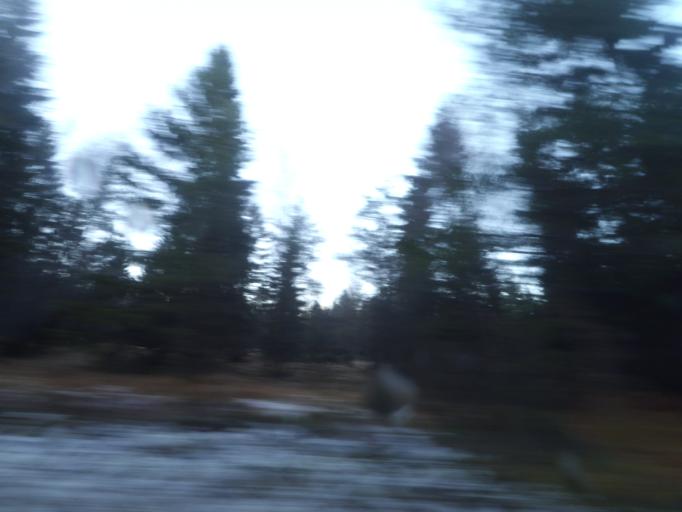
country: DK
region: Central Jutland
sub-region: Ikast-Brande Kommune
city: Brande
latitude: 56.0100
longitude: 9.0637
